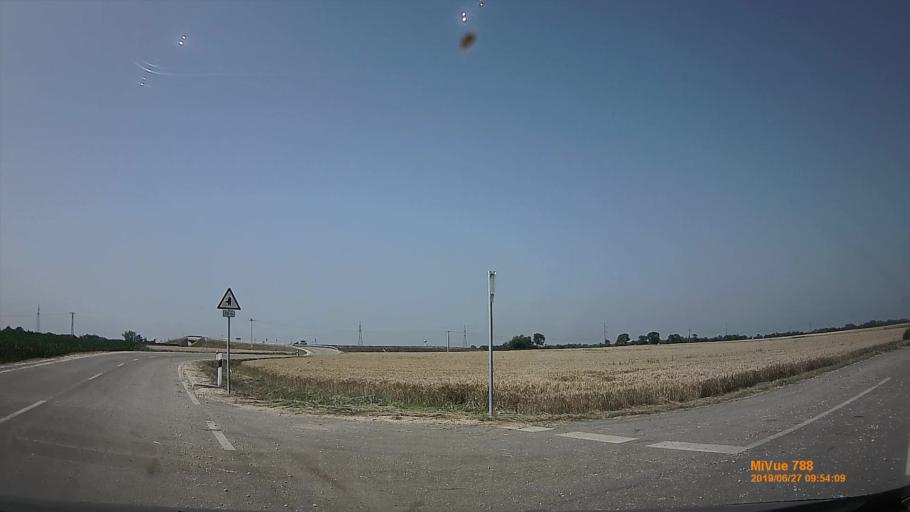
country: HU
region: Pest
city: Cegledbercel
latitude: 47.2169
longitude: 19.7362
